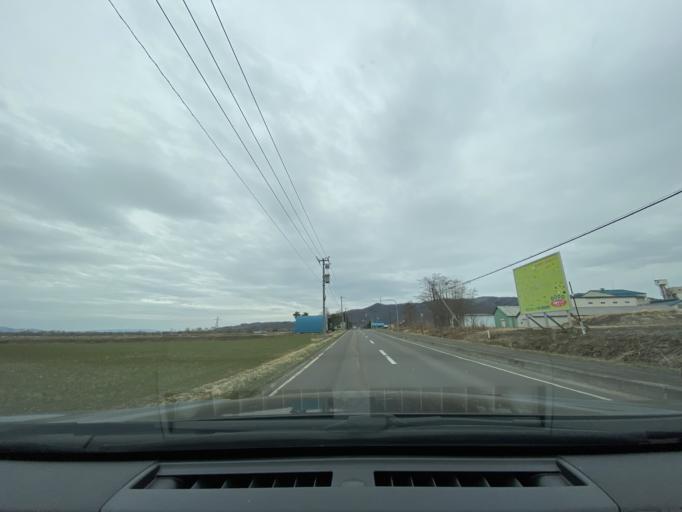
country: JP
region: Hokkaido
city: Nayoro
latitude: 44.1212
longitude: 142.4823
